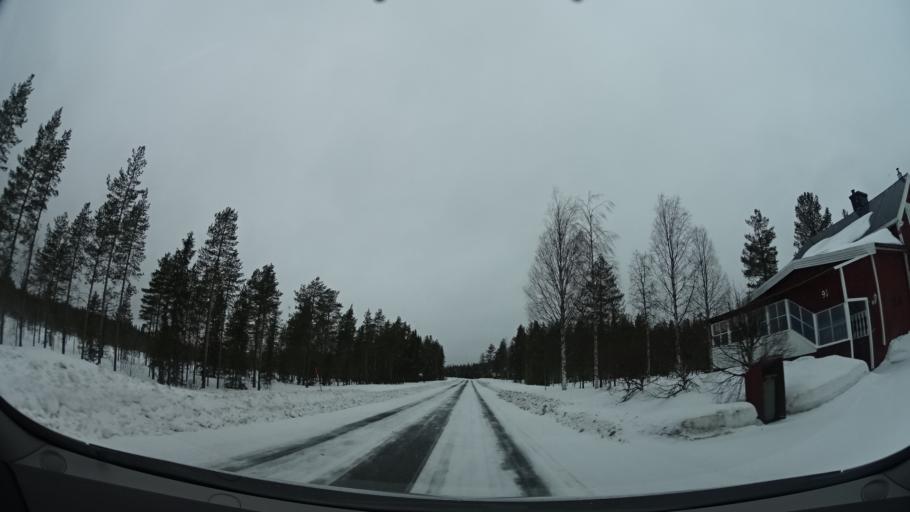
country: SE
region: Vaesterbotten
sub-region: Mala Kommun
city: Mala
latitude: 65.0816
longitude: 18.9991
